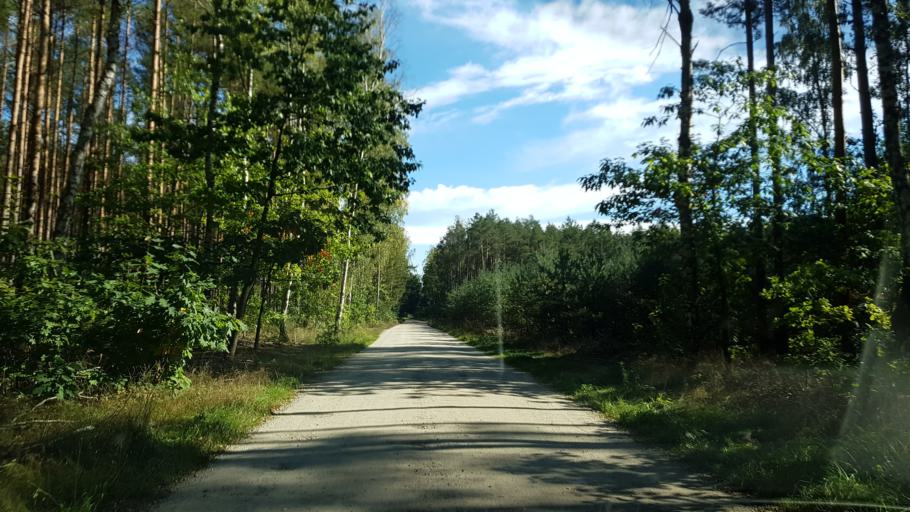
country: PL
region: Lubusz
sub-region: Powiat gorzowski
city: Lubiszyn
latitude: 52.8536
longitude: 14.9412
